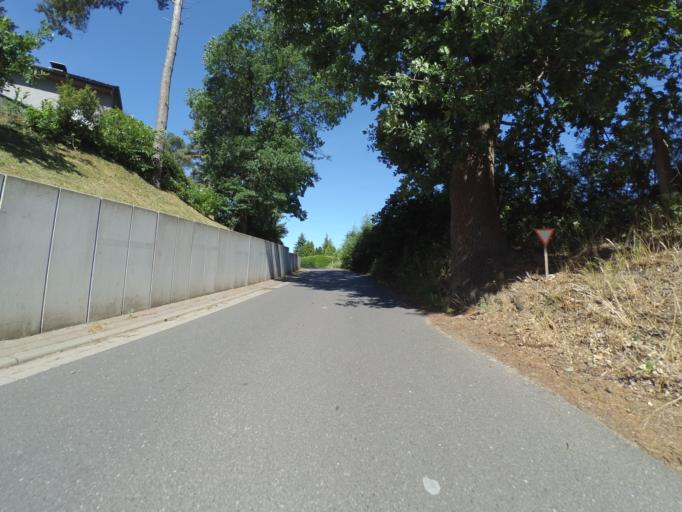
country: DE
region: Mecklenburg-Vorpommern
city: Plau am See
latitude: 53.4889
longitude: 12.2784
